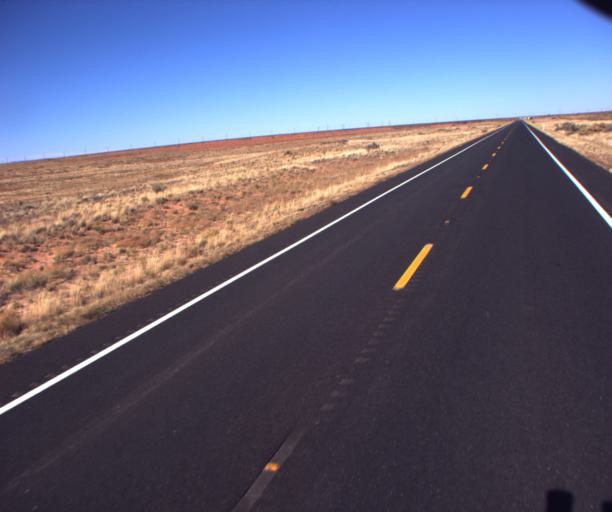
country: US
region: Arizona
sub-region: Coconino County
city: Kaibito
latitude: 36.3821
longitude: -110.8869
